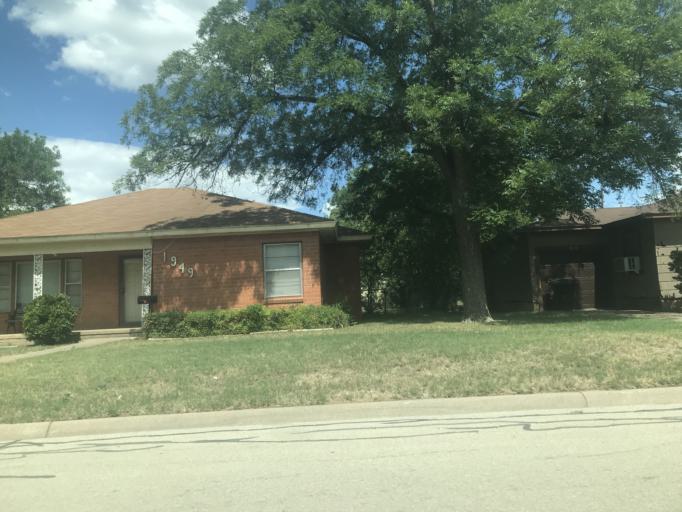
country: US
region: Texas
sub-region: Taylor County
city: Abilene
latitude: 32.4256
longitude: -99.7526
